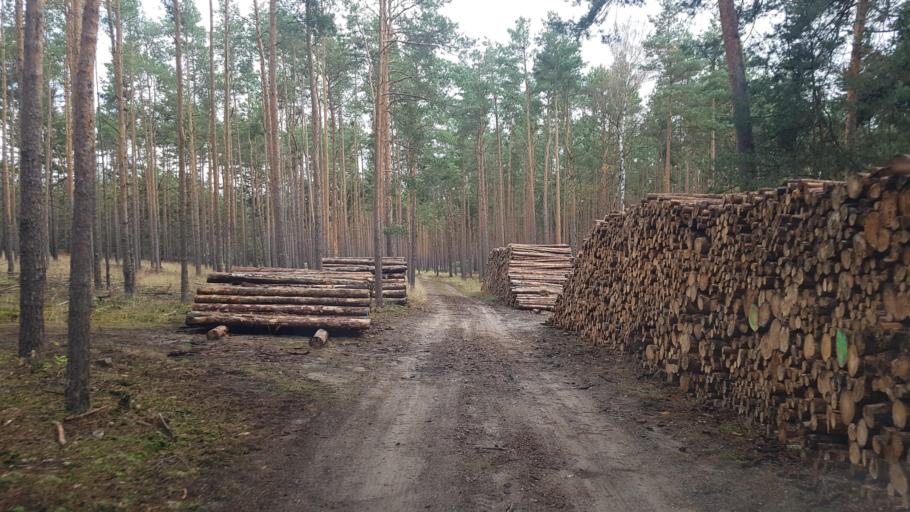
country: DE
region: Brandenburg
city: Elsterwerda
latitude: 51.4871
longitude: 13.4617
